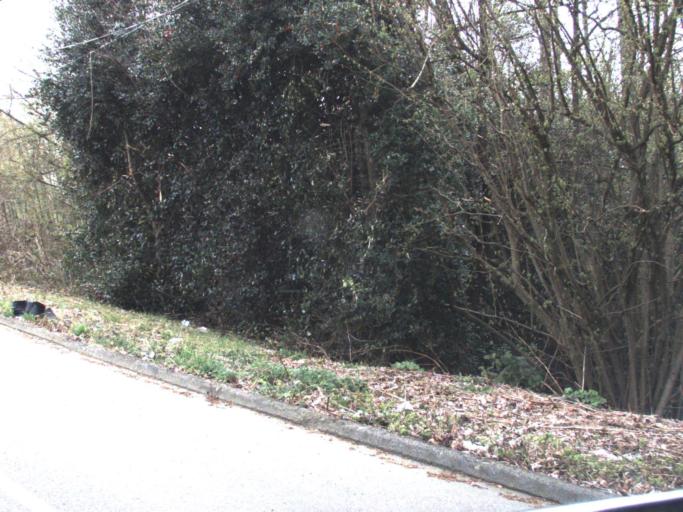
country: US
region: Washington
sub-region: King County
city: Des Moines
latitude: 47.3953
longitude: -122.2974
